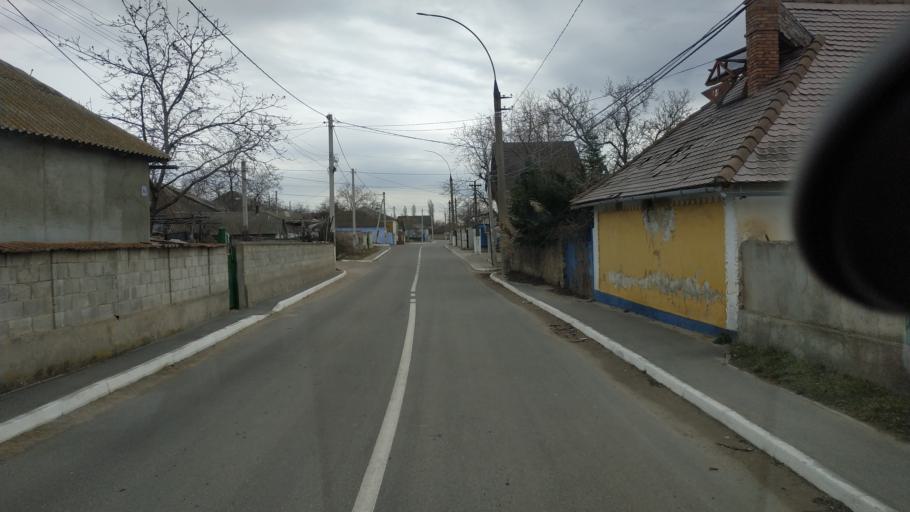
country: MD
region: Telenesti
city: Cocieri
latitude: 47.3482
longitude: 29.1098
